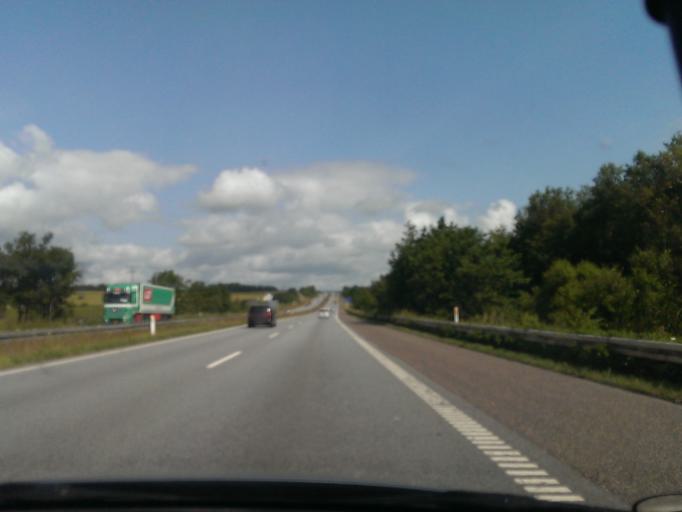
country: DK
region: Central Jutland
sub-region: Randers Kommune
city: Randers
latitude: 56.4776
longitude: 9.9817
